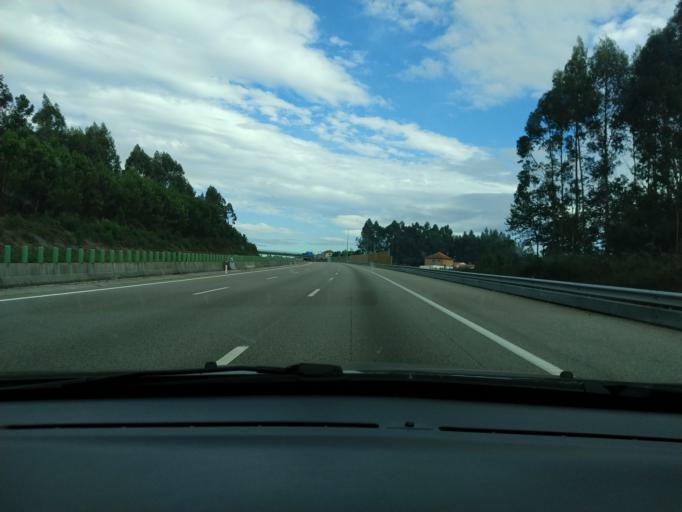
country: PT
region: Aveiro
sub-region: Santa Maria da Feira
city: Feira
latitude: 40.9013
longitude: -8.5670
